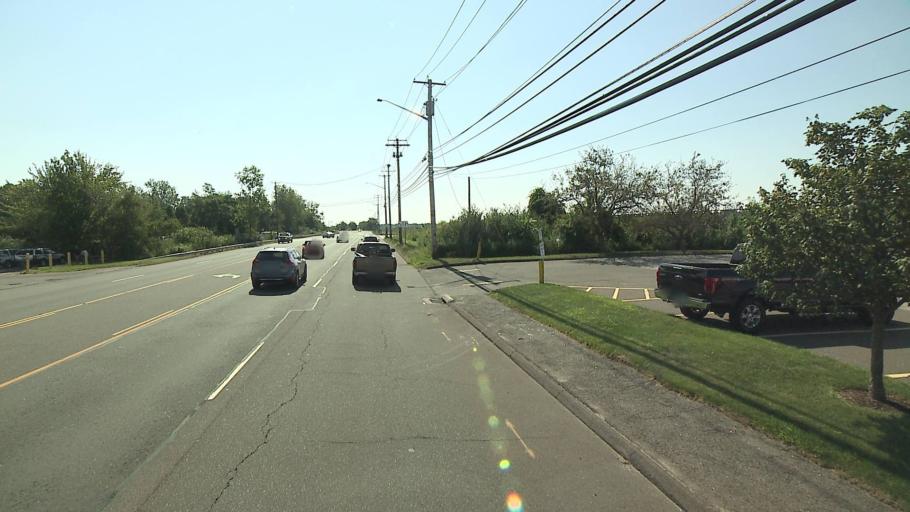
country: US
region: Connecticut
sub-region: Fairfield County
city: Stratford
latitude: 41.1683
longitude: -73.1474
